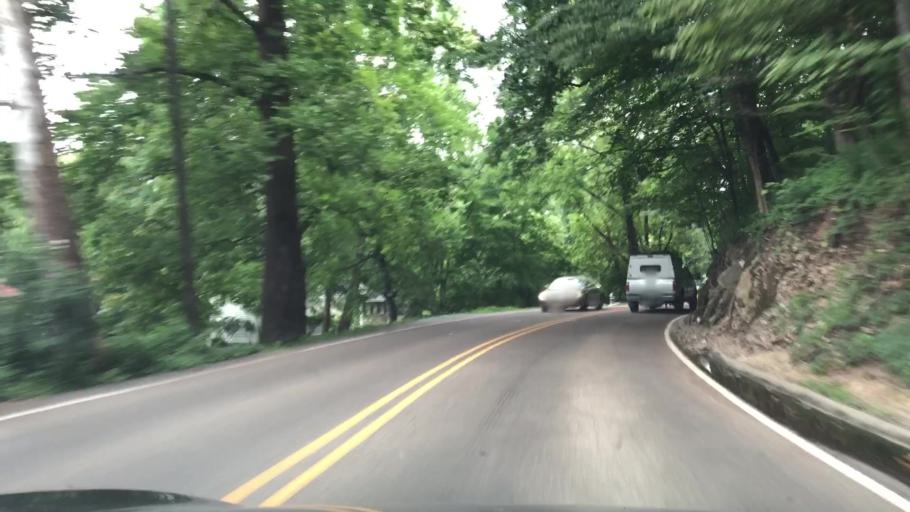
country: US
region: Pennsylvania
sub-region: Chester County
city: Devon
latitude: 40.0634
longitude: -75.4322
